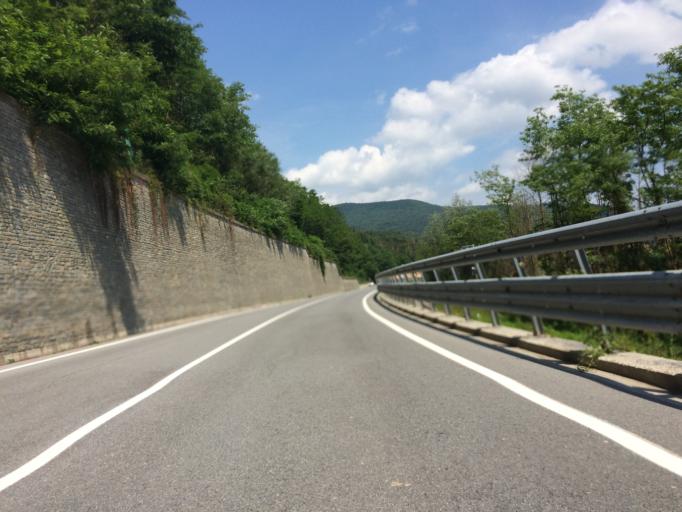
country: IT
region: Piedmont
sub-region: Provincia di Cuneo
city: Priola
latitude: 44.2527
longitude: 8.0206
